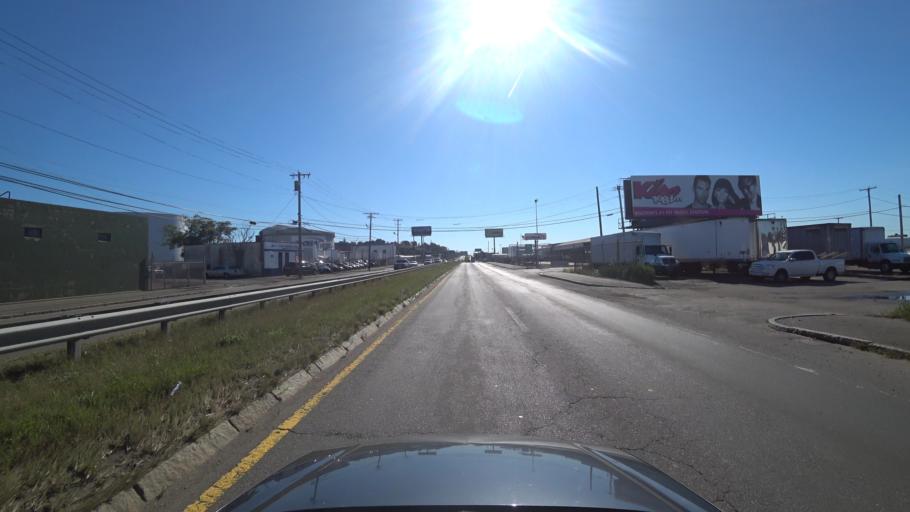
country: US
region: Massachusetts
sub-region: Suffolk County
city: Revere
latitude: 42.3999
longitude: -71.0065
